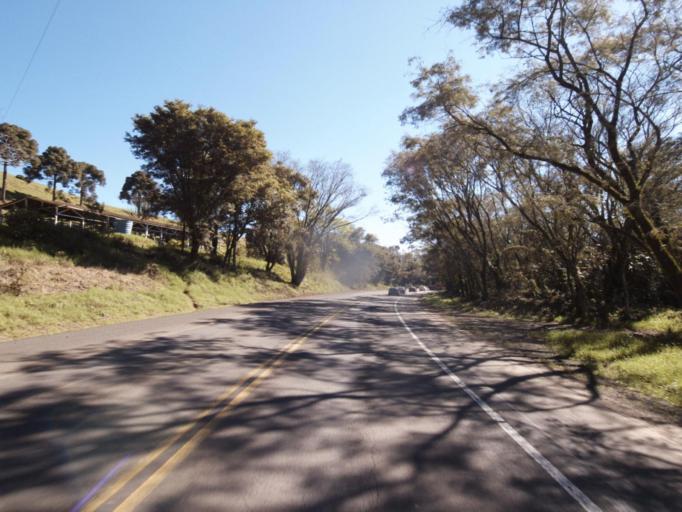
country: BR
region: Rio Grande do Sul
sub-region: Frederico Westphalen
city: Frederico Westphalen
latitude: -26.7927
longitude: -53.4559
